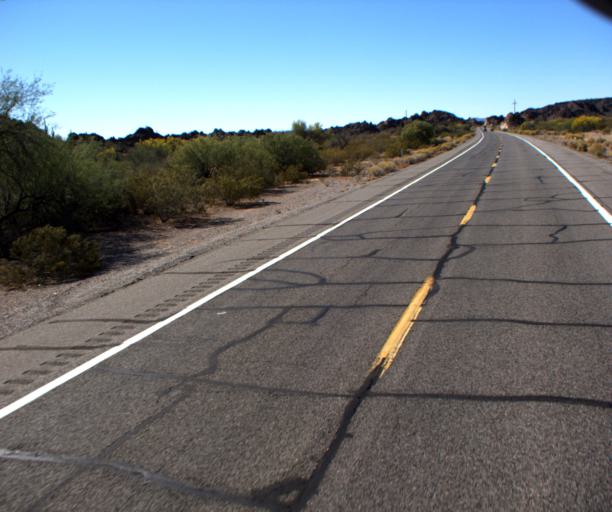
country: US
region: Arizona
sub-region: Pima County
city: Ajo
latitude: 32.5585
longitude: -112.8788
